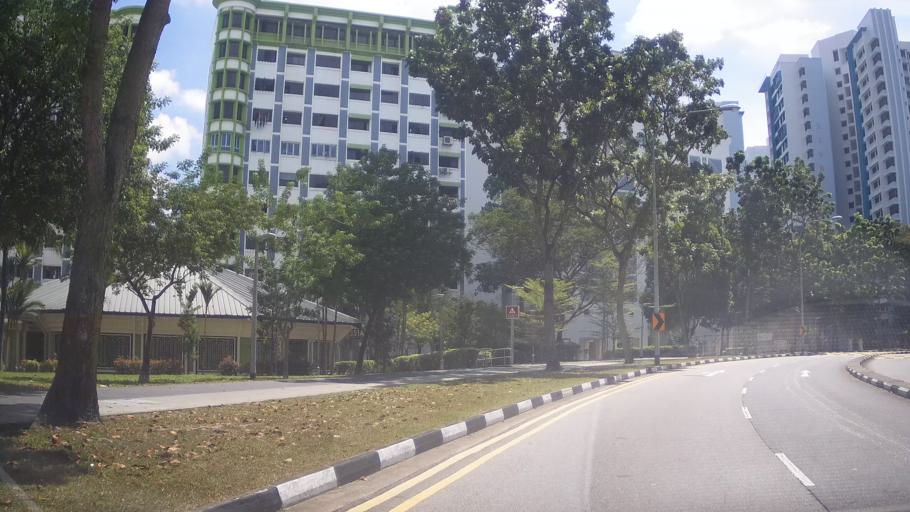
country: MY
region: Johor
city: Johor Bahru
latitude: 1.3387
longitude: 103.7198
